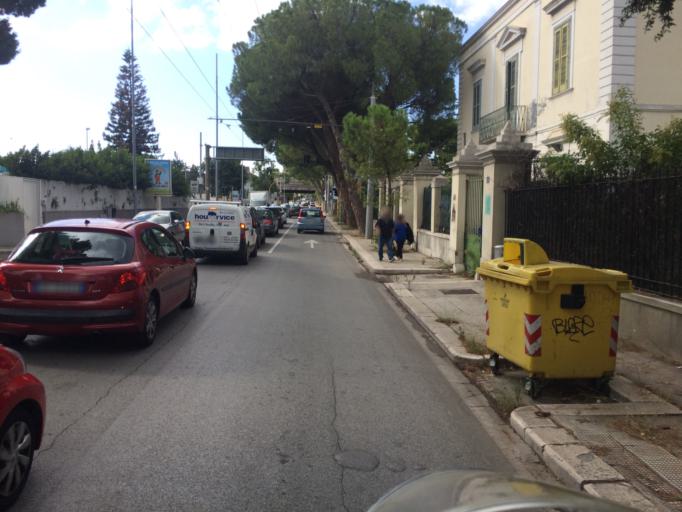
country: IT
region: Apulia
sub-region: Provincia di Bari
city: Bari
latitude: 41.0915
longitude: 16.8700
